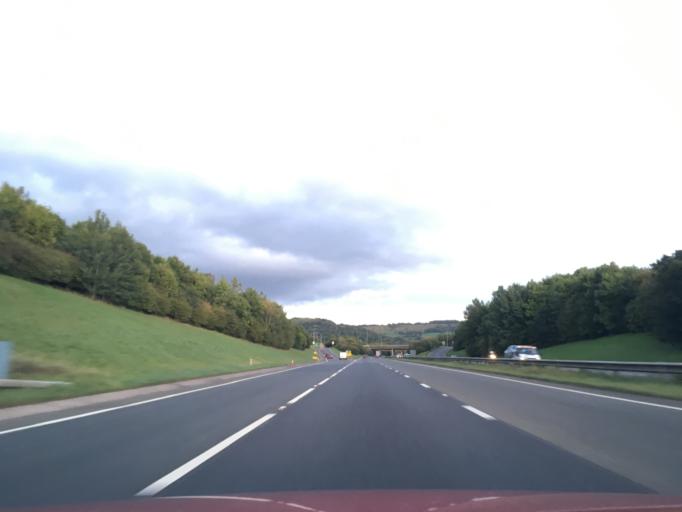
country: GB
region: England
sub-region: Gloucestershire
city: Shurdington
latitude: 51.8517
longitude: -2.1458
